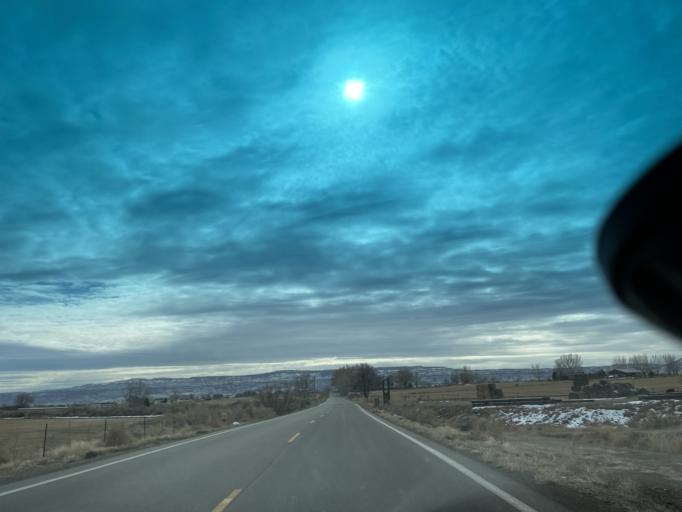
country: US
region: Colorado
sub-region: Mesa County
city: Loma
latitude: 39.2278
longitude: -108.8130
